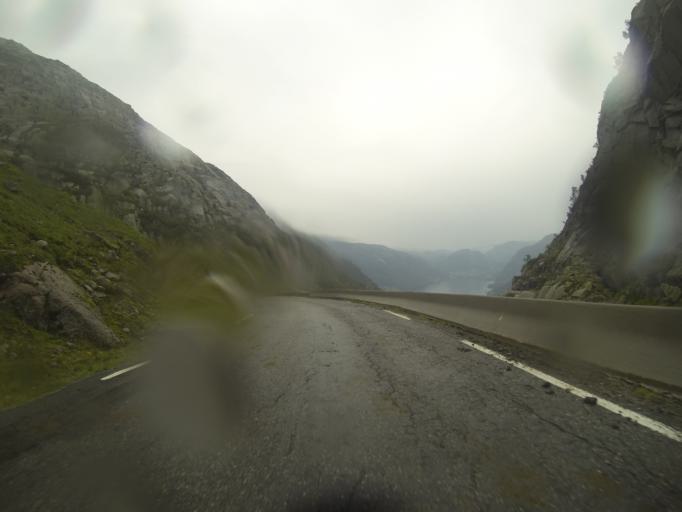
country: NO
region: Hordaland
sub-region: Odda
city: Odda
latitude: 59.7794
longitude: 6.7525
